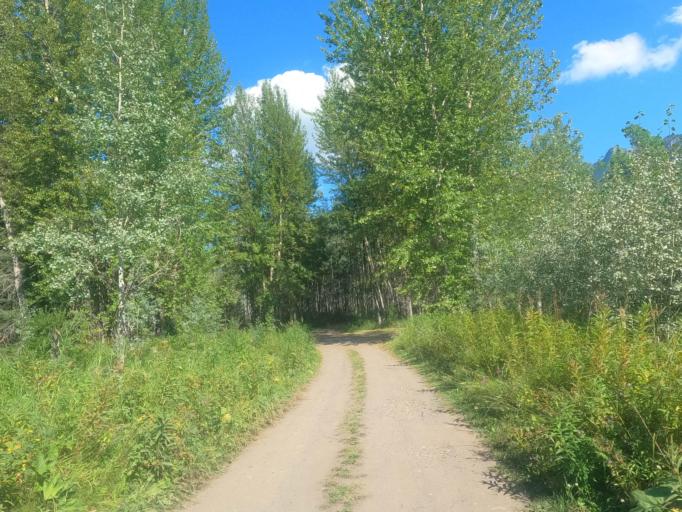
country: CA
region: British Columbia
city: Houston
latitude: 54.2862
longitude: -126.8557
